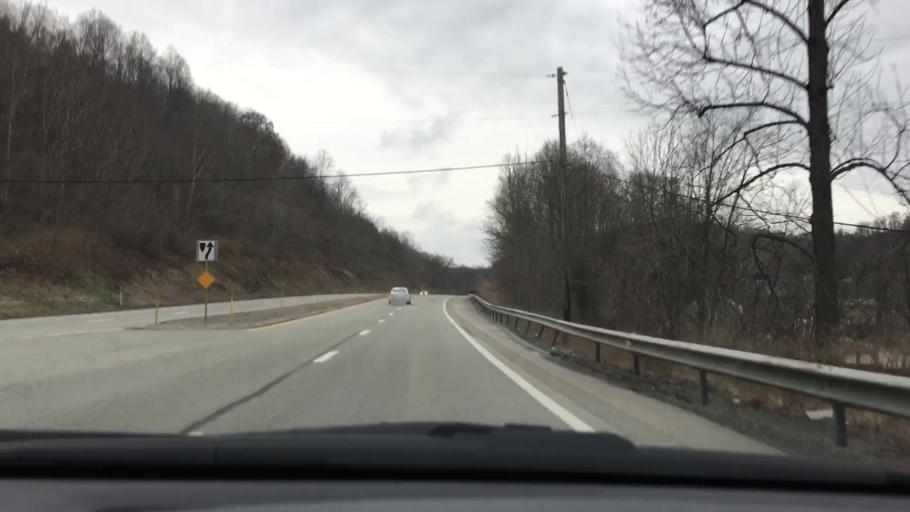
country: US
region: Pennsylvania
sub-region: Fayette County
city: Oliver
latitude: 39.9937
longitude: -79.7647
